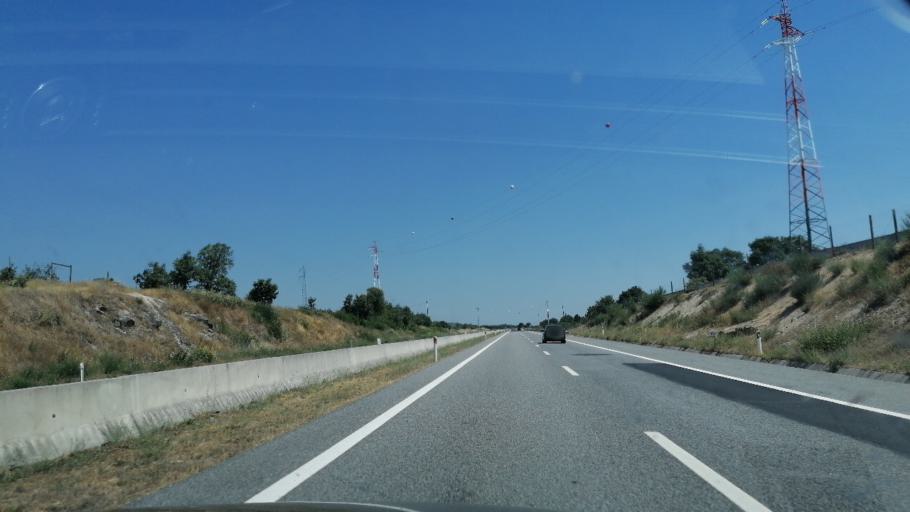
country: PT
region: Braganca
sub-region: Braganca Municipality
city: Braganca
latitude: 41.6844
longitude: -6.8157
